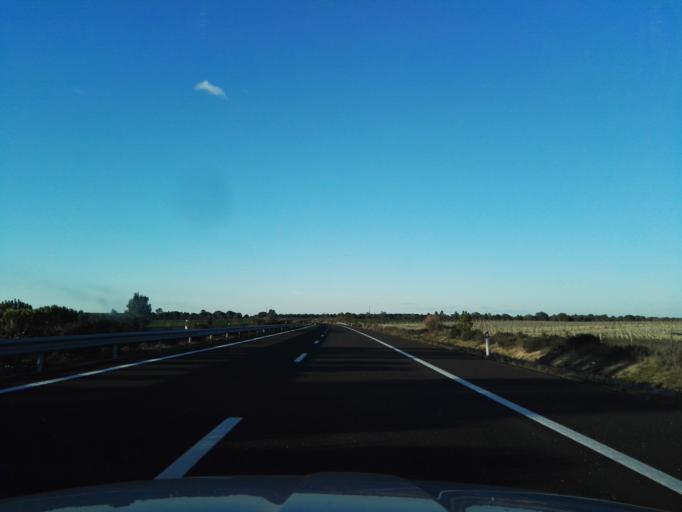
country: PT
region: Santarem
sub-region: Benavente
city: Poceirao
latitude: 38.7772
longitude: -8.6837
